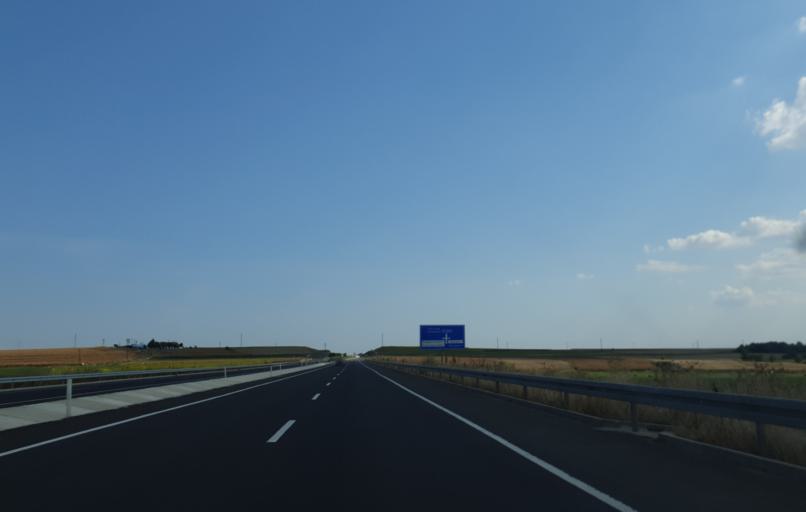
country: TR
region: Tekirdag
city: Muratli
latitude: 41.2160
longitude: 27.5330
